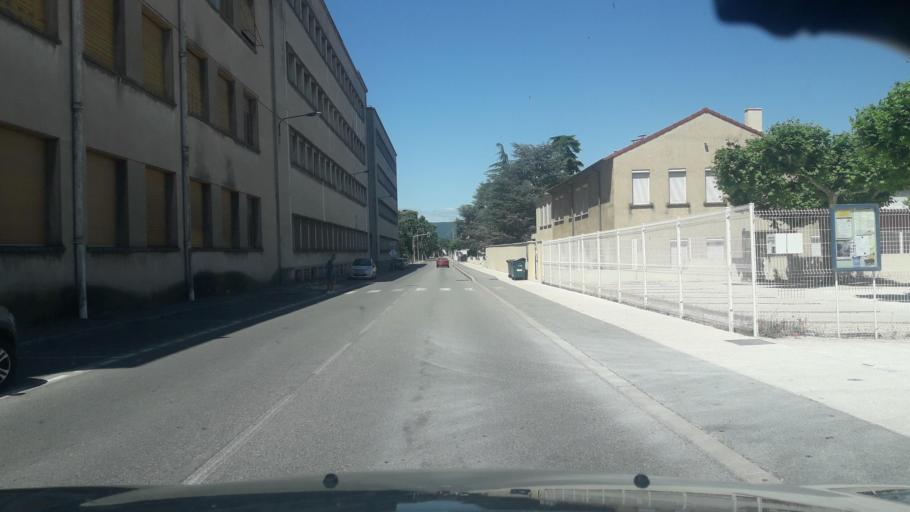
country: FR
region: Rhone-Alpes
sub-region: Departement de la Drome
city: Livron-sur-Drome
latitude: 44.7734
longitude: 4.8432
